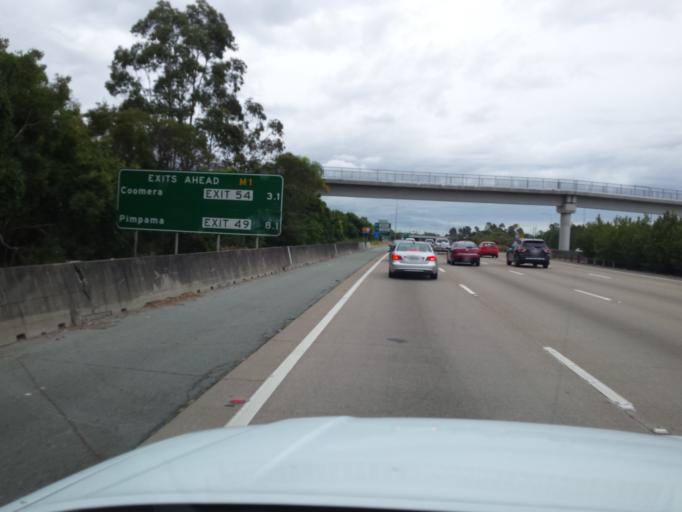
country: AU
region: Queensland
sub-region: Gold Coast
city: Oxenford
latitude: -27.8909
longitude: 153.3145
